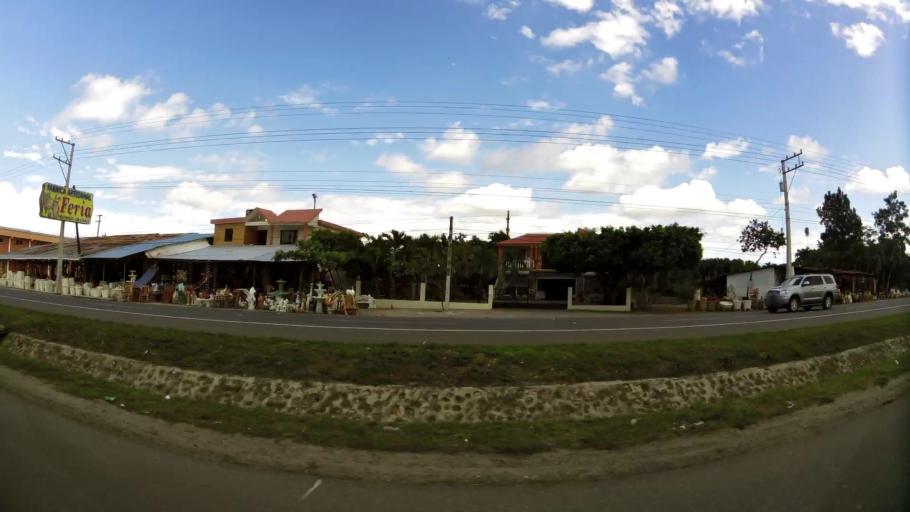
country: DO
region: La Vega
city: Rio Verde Arriba
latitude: 19.3563
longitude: -70.6012
